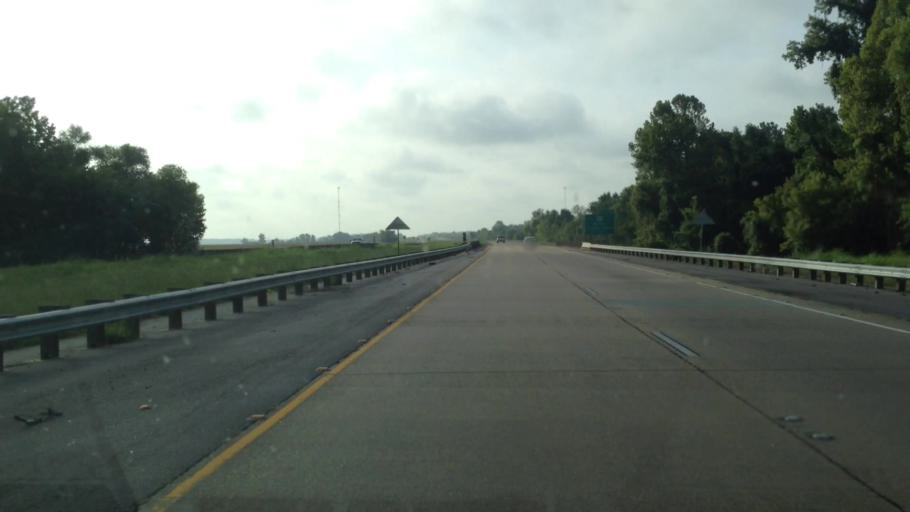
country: US
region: Louisiana
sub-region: Rapides Parish
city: Lecompte
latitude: 31.0204
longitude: -92.3902
